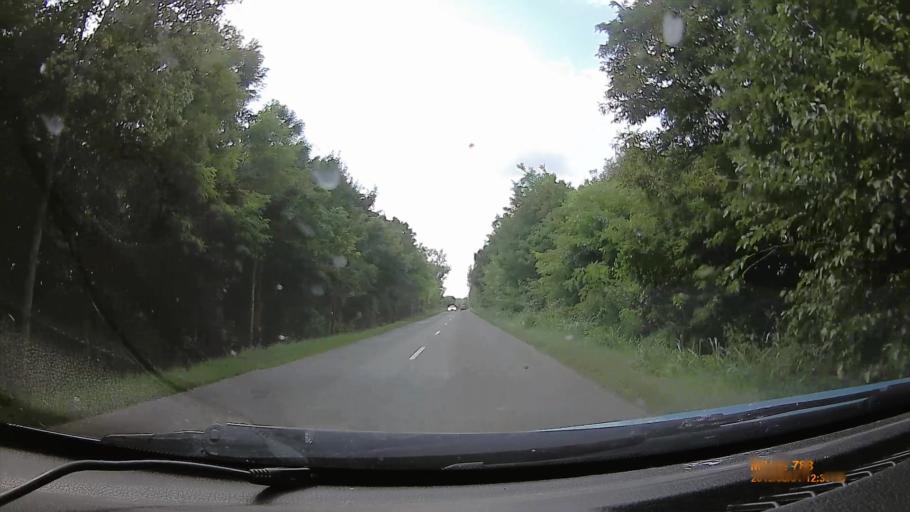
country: HU
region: Baranya
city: Harkany
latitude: 45.8390
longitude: 18.1935
